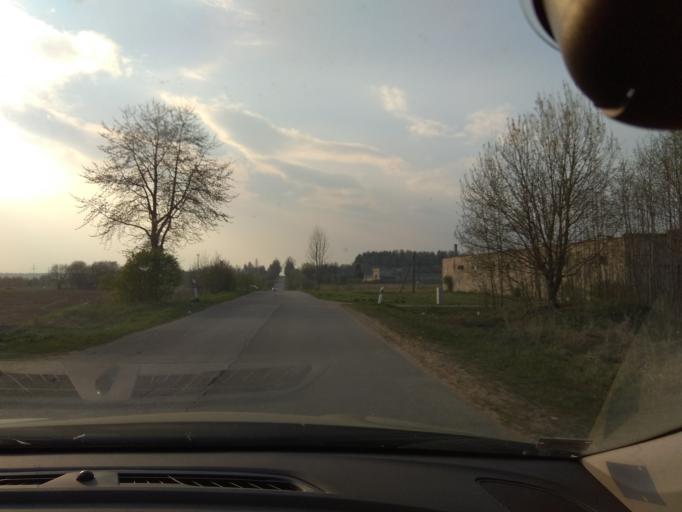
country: LT
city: Baltoji Voke
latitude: 54.5947
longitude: 25.1521
